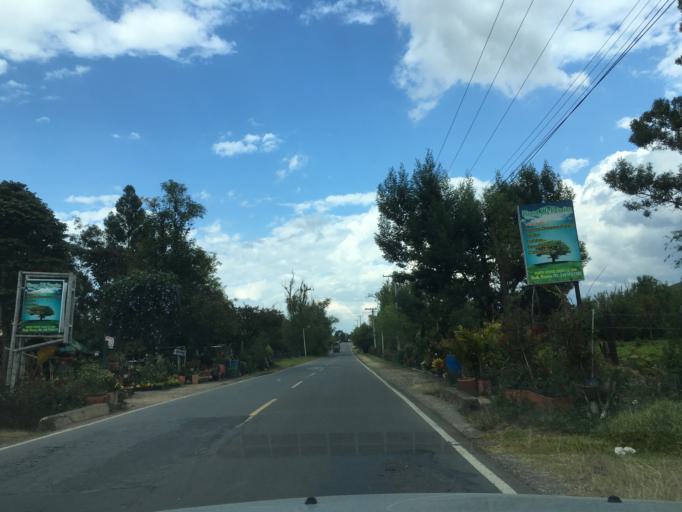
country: CO
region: Boyaca
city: Sutamarchan
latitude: 5.6077
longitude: -73.6325
